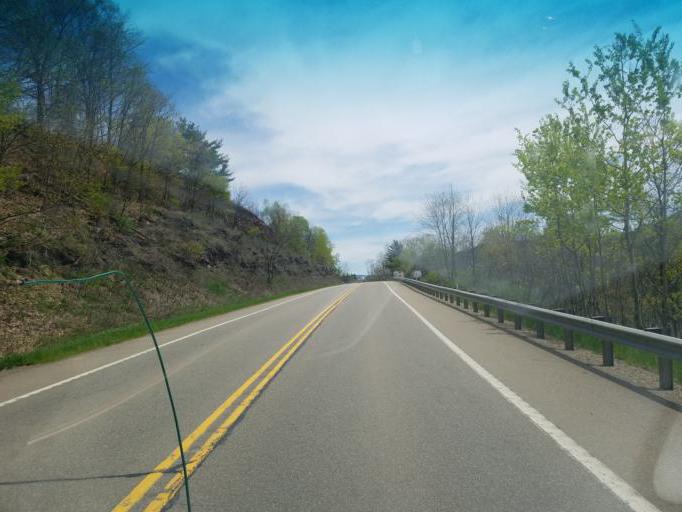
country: US
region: Pennsylvania
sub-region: Potter County
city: Galeton
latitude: 41.7430
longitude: -77.6118
